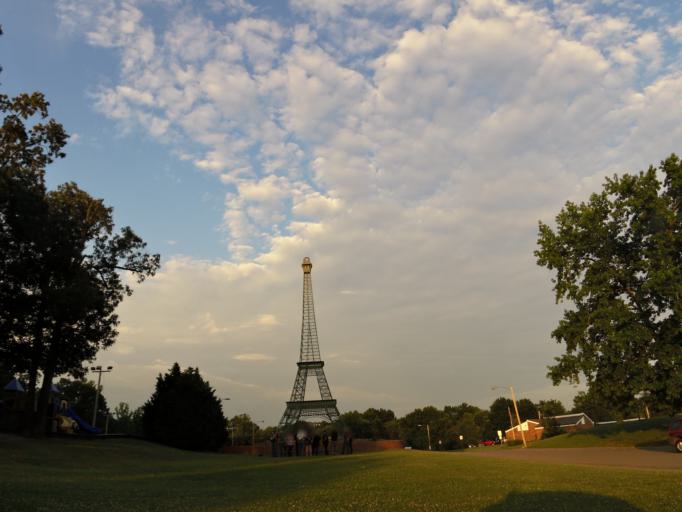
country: US
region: Tennessee
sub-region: Henry County
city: Paris
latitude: 36.2870
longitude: -88.3020
